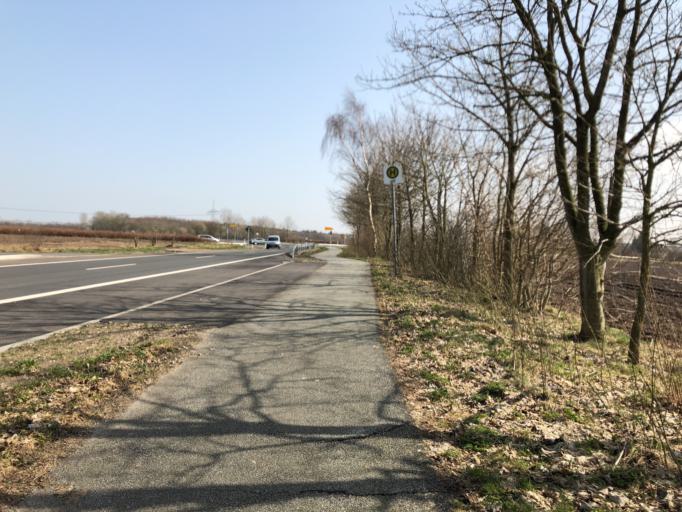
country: DE
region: Schleswig-Holstein
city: Jerrishoe
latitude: 54.6758
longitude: 9.3718
